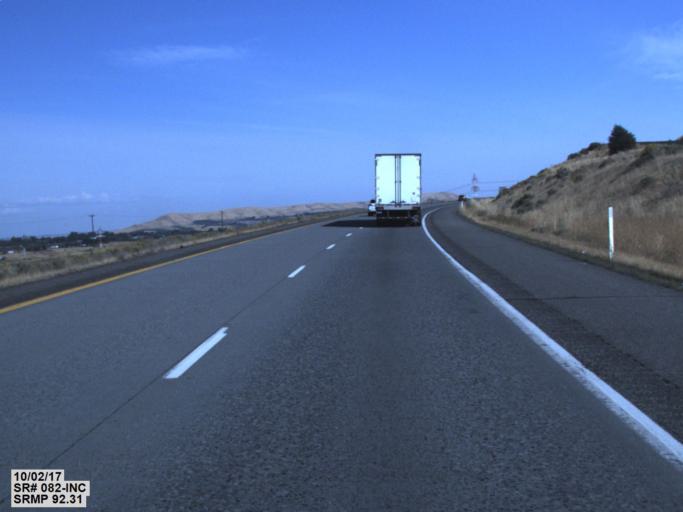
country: US
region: Washington
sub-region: Benton County
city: Benton City
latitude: 46.2671
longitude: -119.5609
